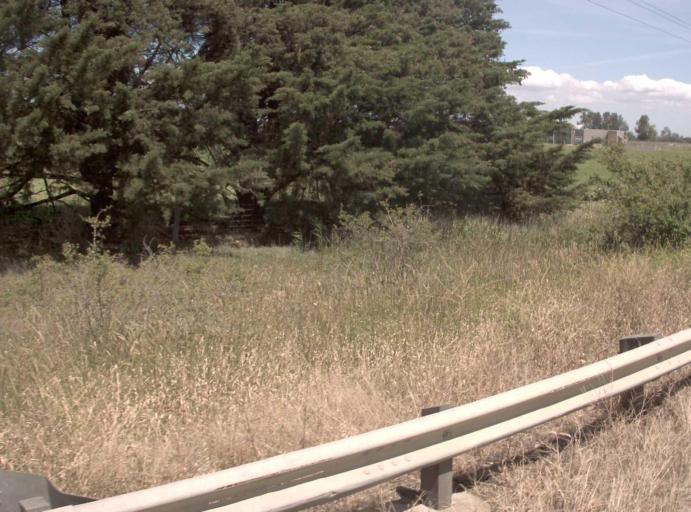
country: AU
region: Victoria
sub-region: Wellington
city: Heyfield
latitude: -37.9926
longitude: 146.8859
